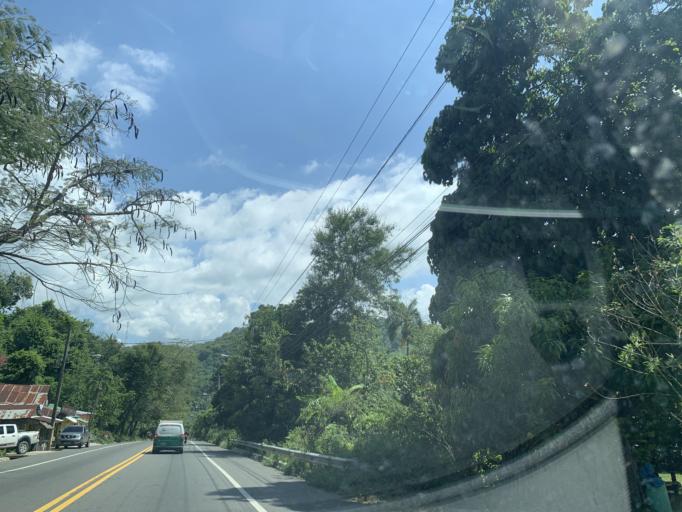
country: DO
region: Puerto Plata
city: Altamira
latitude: 19.7005
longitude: -70.8396
